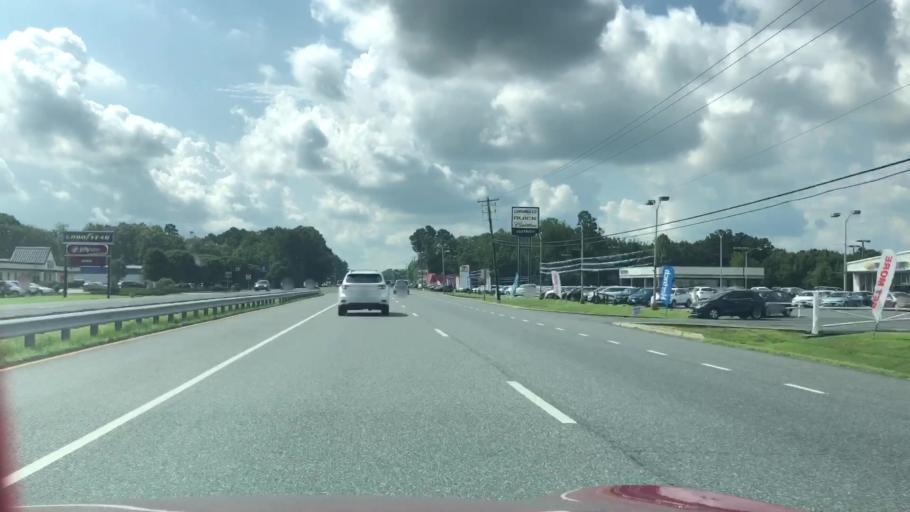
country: US
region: Maryland
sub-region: Worcester County
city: Pocomoke City
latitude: 38.0457
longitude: -75.5430
